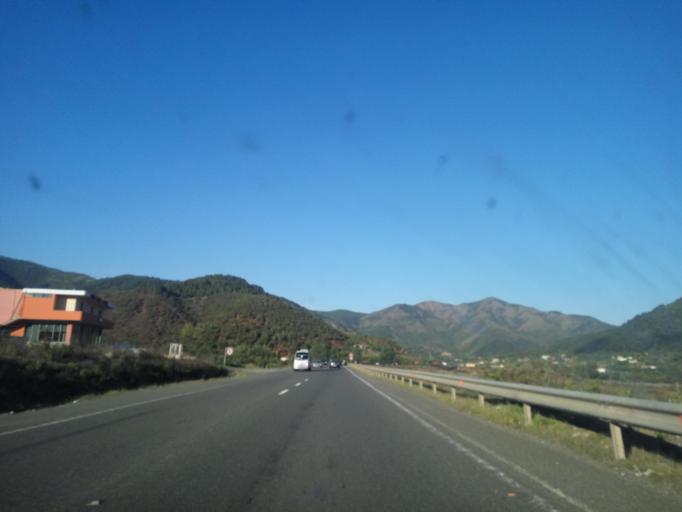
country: AL
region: Lezhe
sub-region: Rrethi i Mirdites
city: Rubik
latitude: 41.7882
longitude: 19.7903
